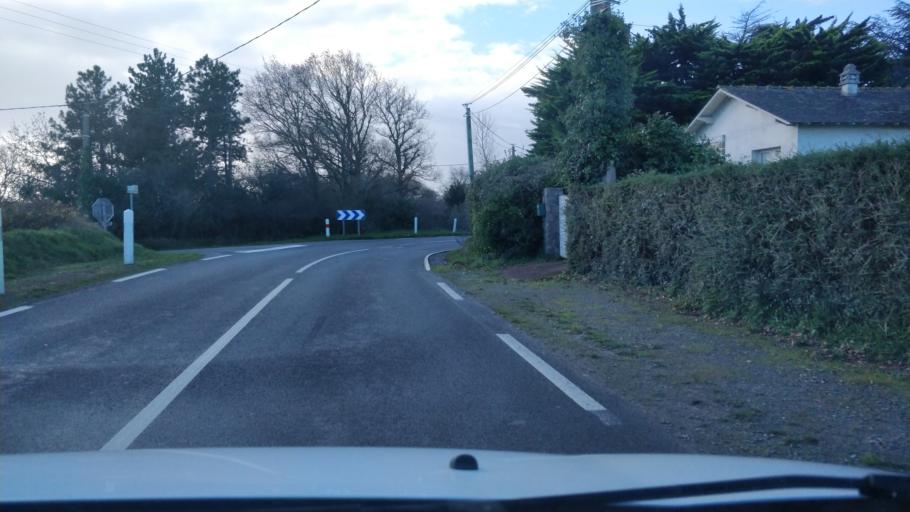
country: FR
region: Pays de la Loire
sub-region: Departement de la Loire-Atlantique
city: Asserac
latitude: 47.4208
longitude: -2.3962
